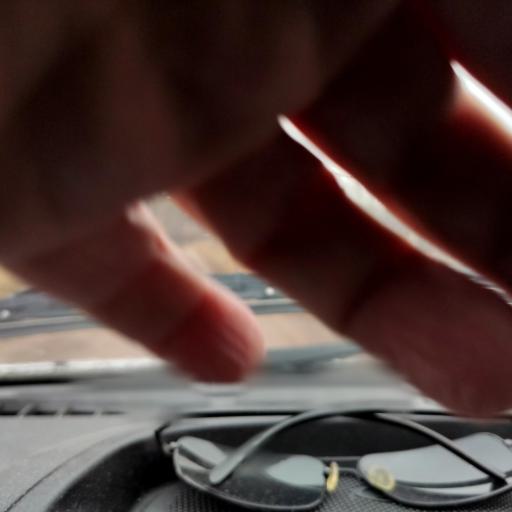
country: RU
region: Samara
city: Zhigulevsk
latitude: 53.5380
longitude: 49.5545
